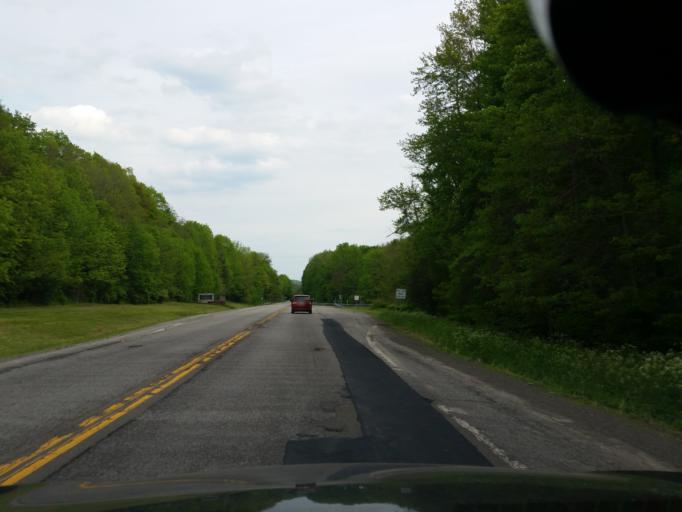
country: US
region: New York
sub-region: Chautauqua County
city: Lakewood
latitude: 42.1814
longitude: -79.4036
